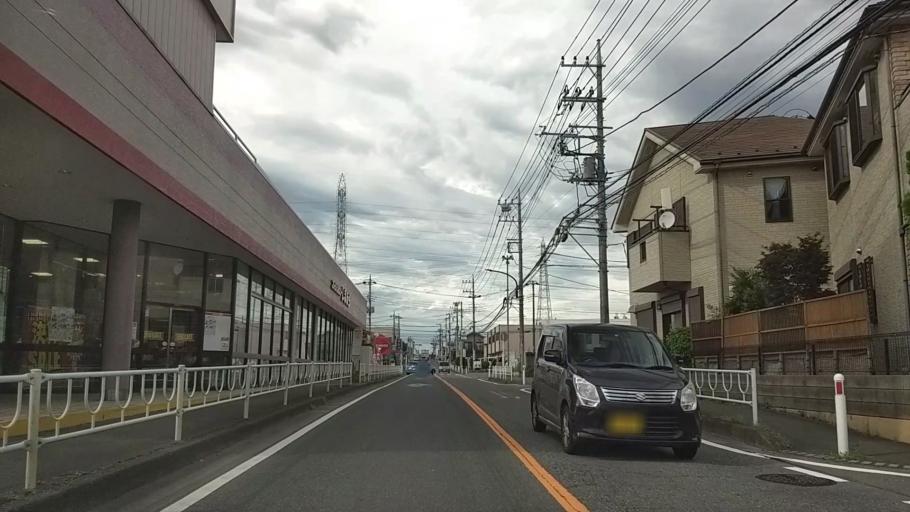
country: JP
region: Tokyo
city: Hachioji
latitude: 35.5887
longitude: 139.3212
